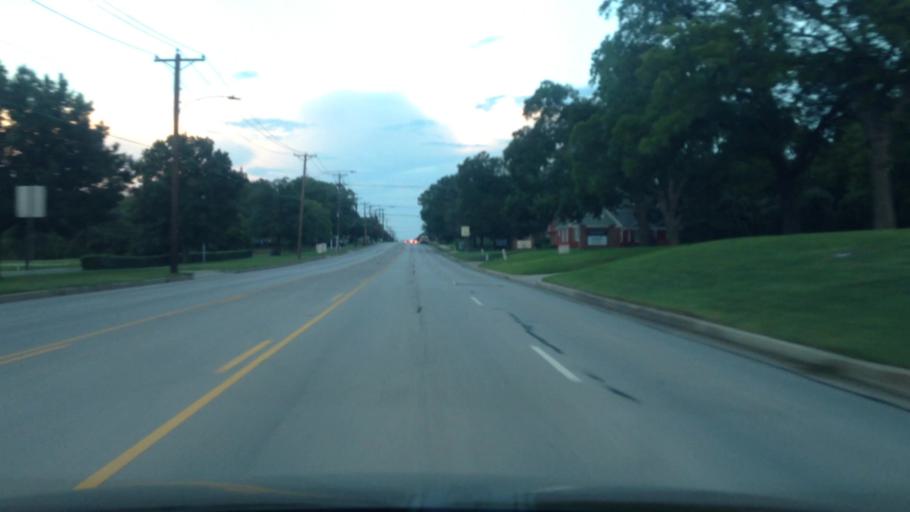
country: US
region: Texas
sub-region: Tarrant County
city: Arlington
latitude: 32.7358
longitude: -97.1293
